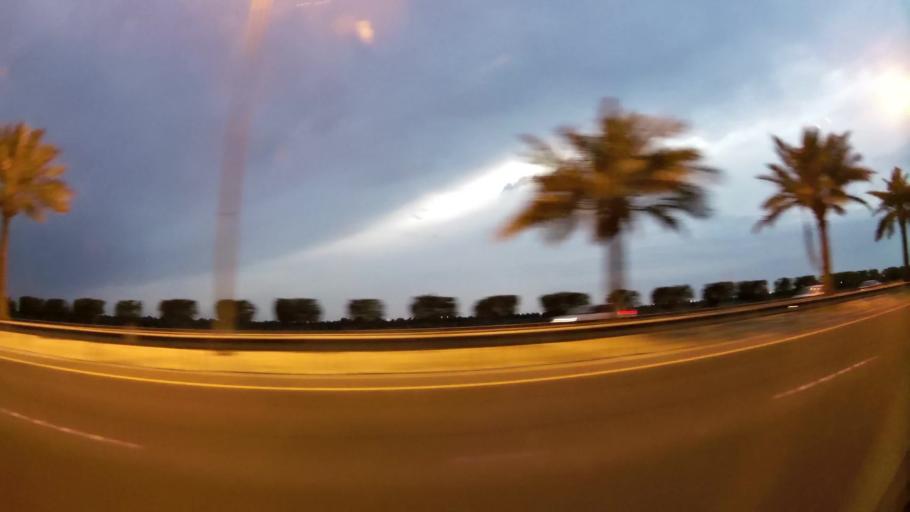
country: BH
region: Northern
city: Madinat `Isa
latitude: 26.1603
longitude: 50.5049
